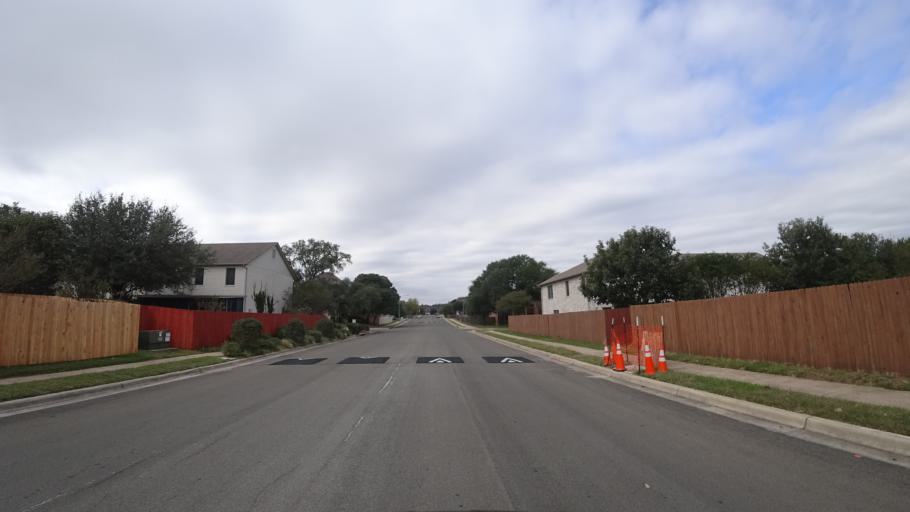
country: US
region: Texas
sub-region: Travis County
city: Manchaca
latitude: 30.1579
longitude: -97.8411
